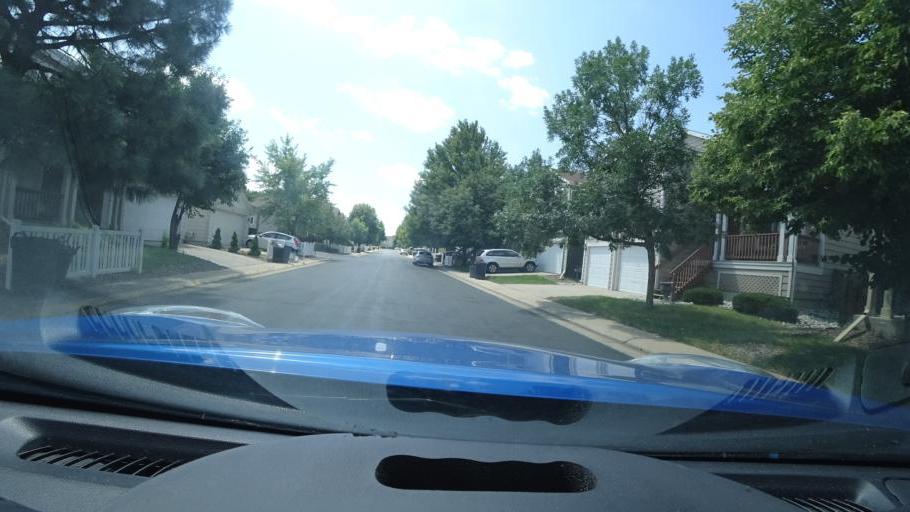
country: US
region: Colorado
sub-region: Arapahoe County
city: Glendale
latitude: 39.6944
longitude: -104.8819
